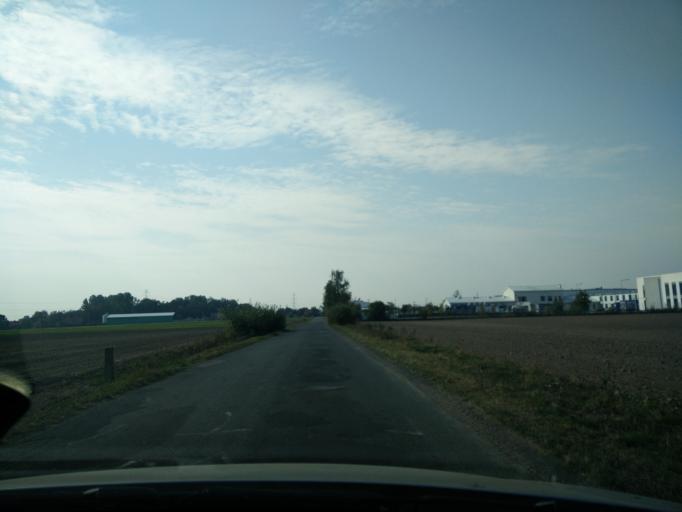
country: PL
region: Greater Poland Voivodeship
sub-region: Powiat sredzki
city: Dominowo
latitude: 52.3068
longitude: 17.2952
